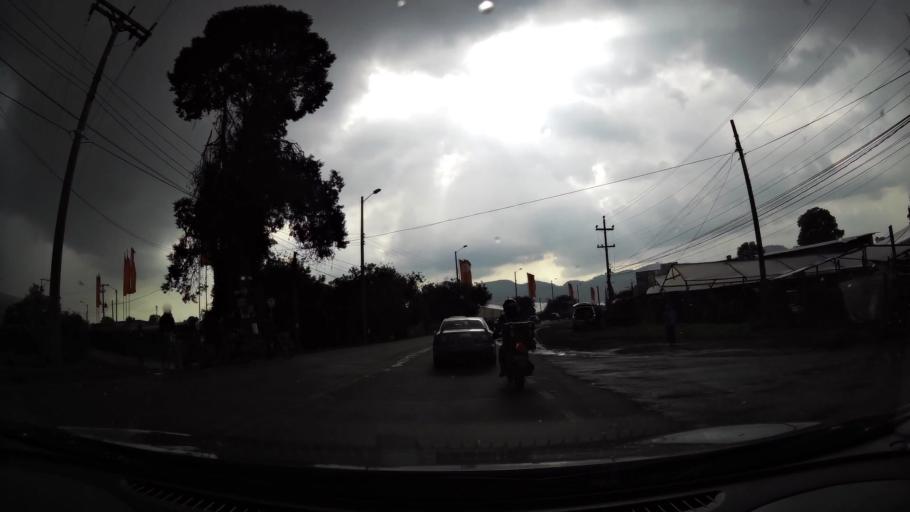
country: CO
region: Cundinamarca
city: Chia
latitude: 4.8482
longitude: -74.0529
